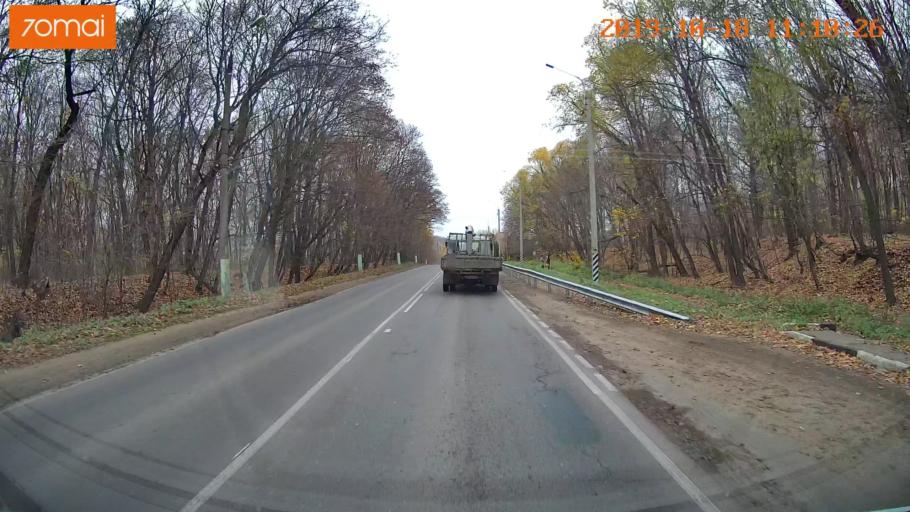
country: RU
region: Tula
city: Kimovsk
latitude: 53.9554
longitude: 38.5389
